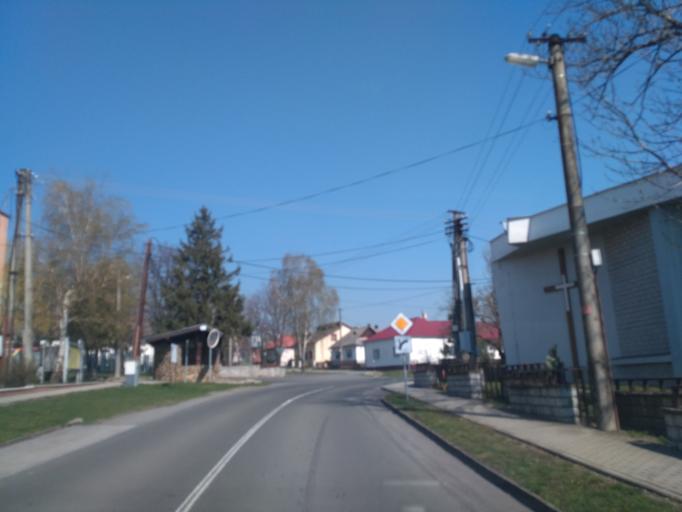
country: SK
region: Kosicky
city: Secovce
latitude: 48.7588
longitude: 21.6420
